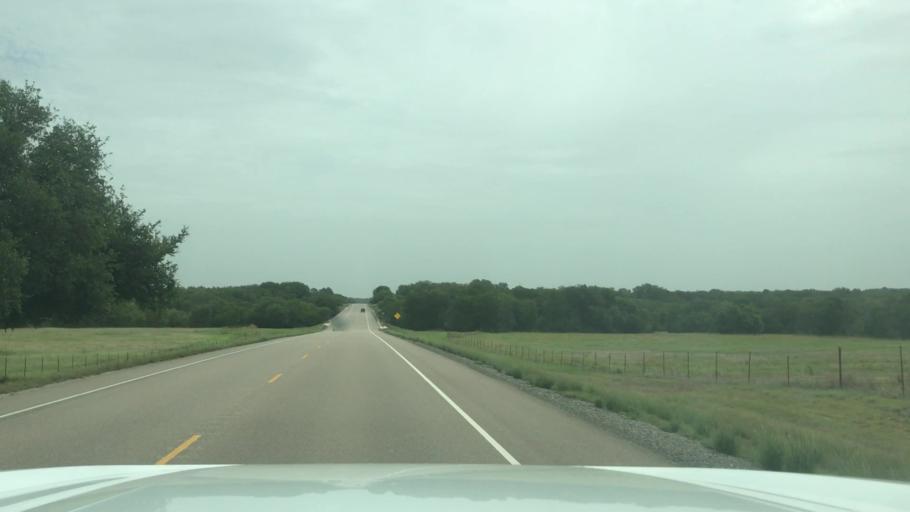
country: US
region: Texas
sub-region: Hamilton County
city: Hico
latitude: 31.9778
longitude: -97.8995
